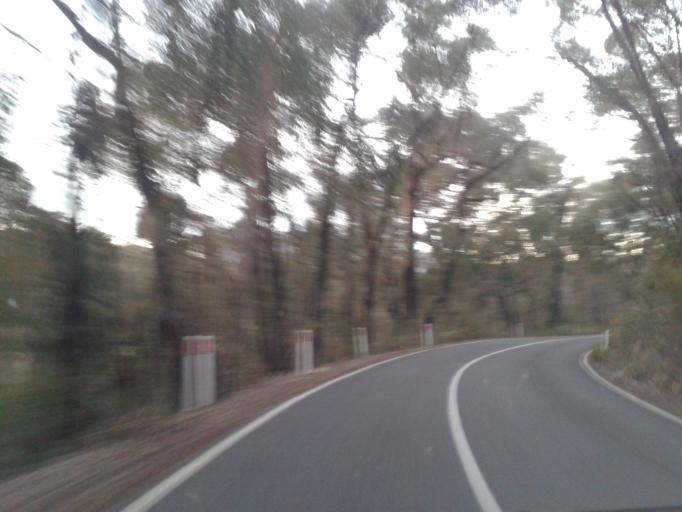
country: AU
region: Victoria
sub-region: Northern Grampians
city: Stawell
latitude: -37.1581
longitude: 142.4968
